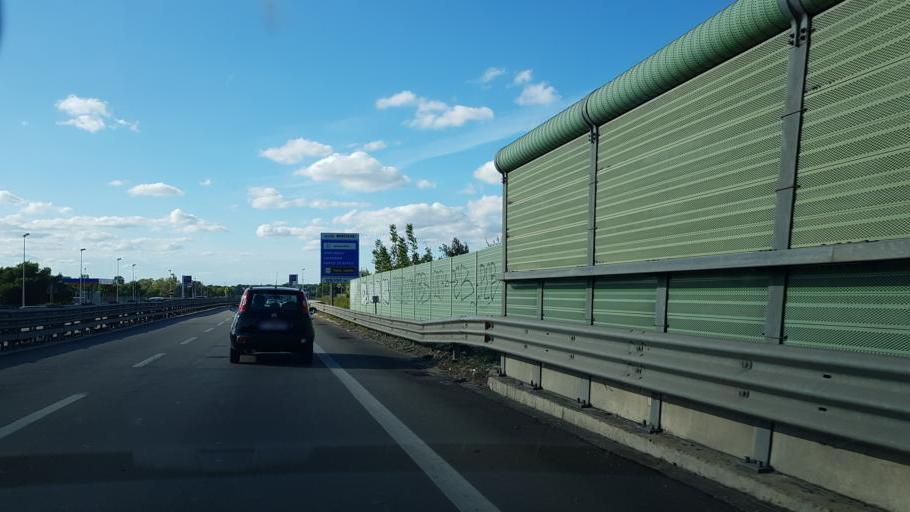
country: IT
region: Apulia
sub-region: Provincia di Lecce
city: Lequile
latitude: 40.3307
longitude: 18.1395
